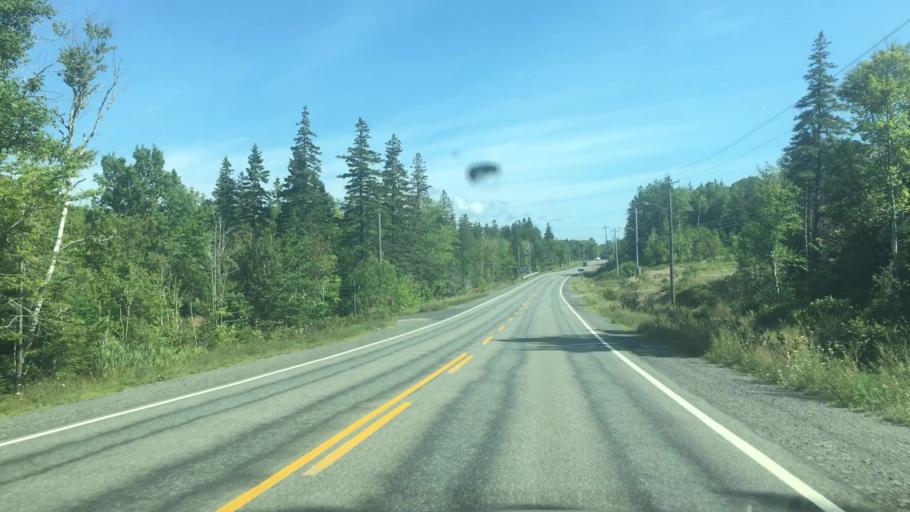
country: CA
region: Nova Scotia
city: Sydney
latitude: 45.9923
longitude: -60.4107
